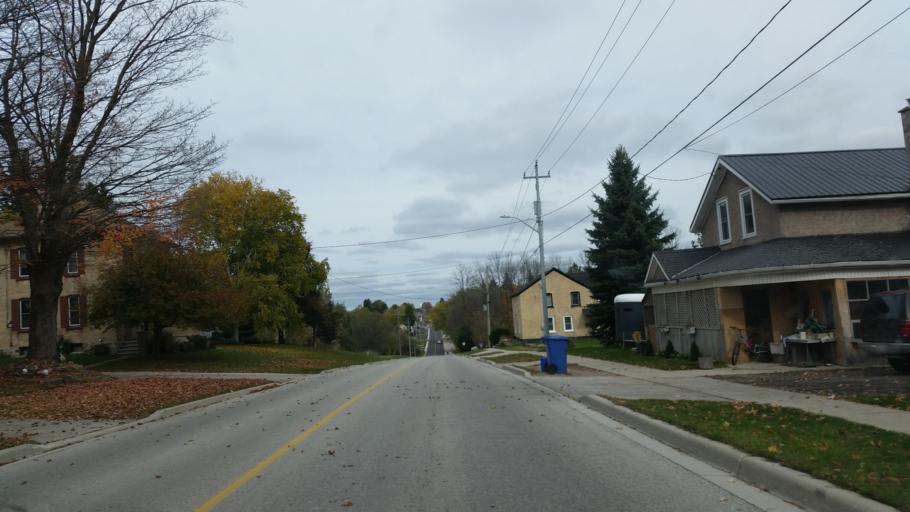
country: CA
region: Ontario
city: Hanover
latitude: 44.0380
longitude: -81.1234
